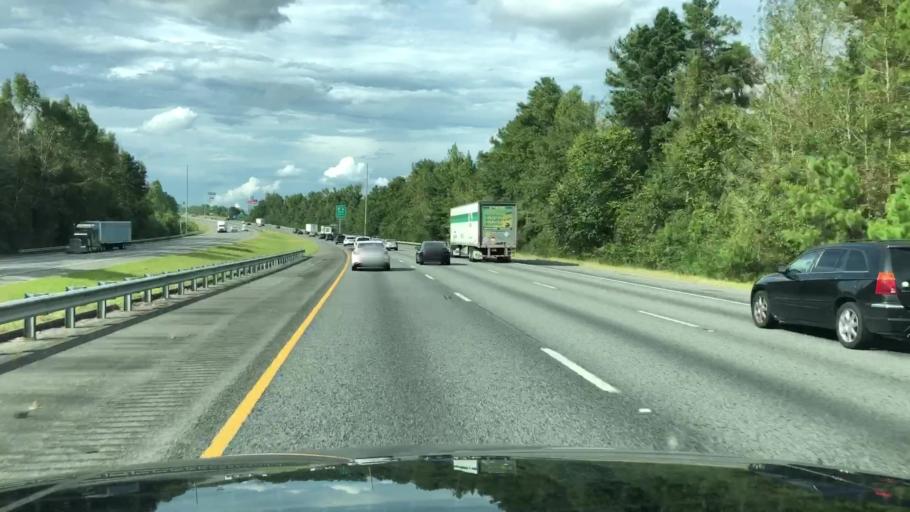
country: US
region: Georgia
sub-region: Bibb County
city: West Point
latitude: 32.7978
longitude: -83.7199
